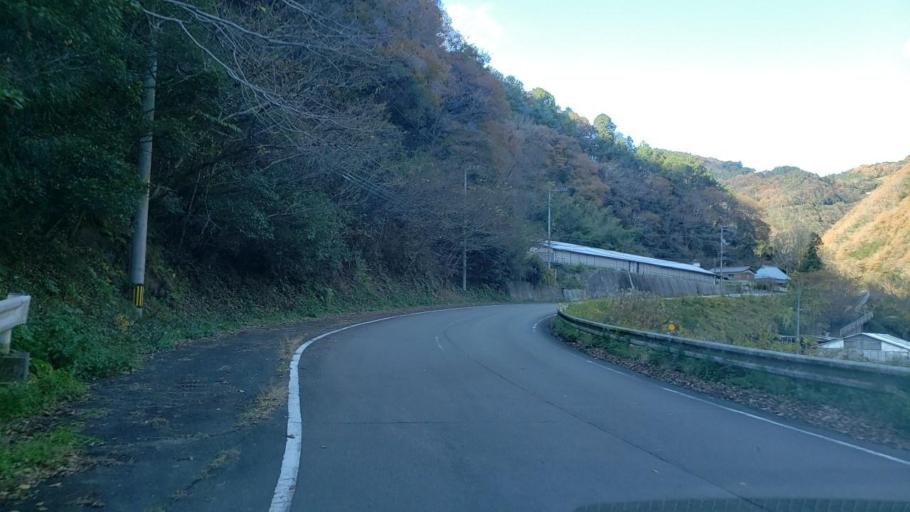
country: JP
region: Tokushima
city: Wakimachi
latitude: 34.0833
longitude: 134.0727
